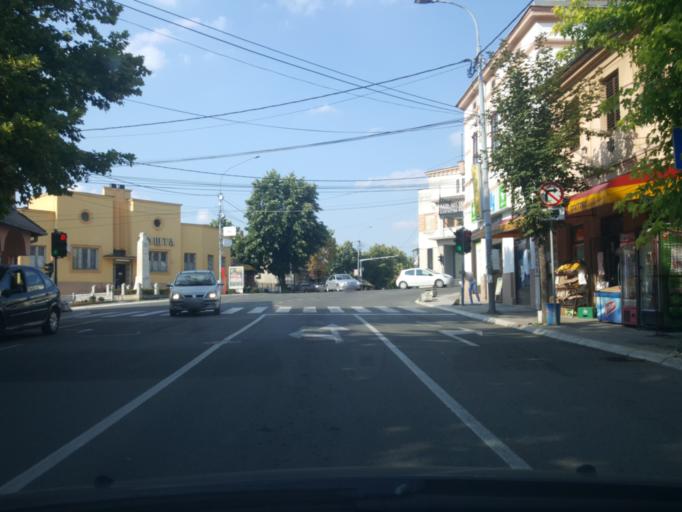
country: RS
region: Central Serbia
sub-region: Sumadijski Okrug
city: Topola
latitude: 44.2543
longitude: 20.6780
